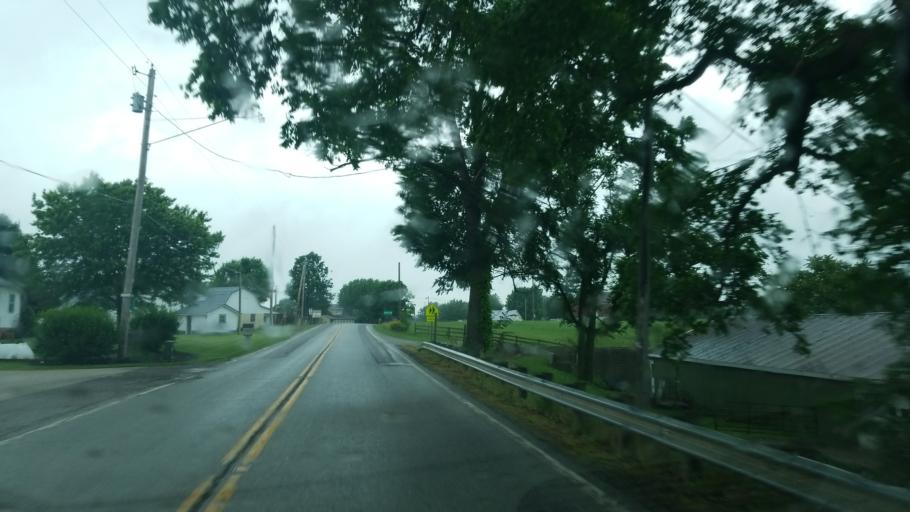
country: US
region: Ohio
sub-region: Tuscarawas County
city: Sugarcreek
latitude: 40.4833
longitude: -81.7258
